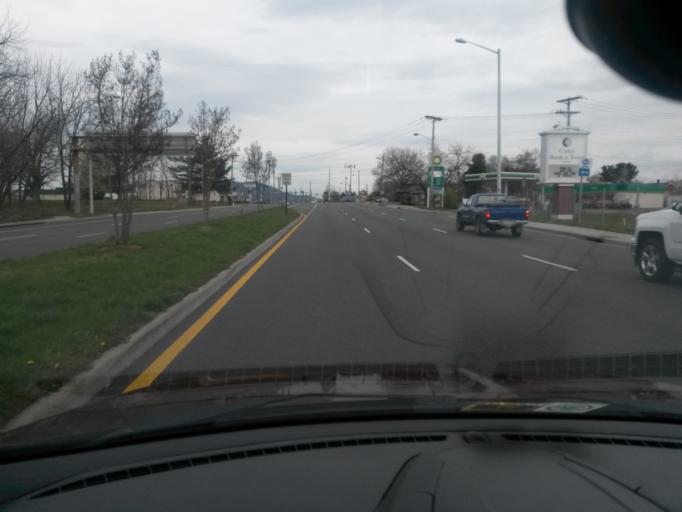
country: US
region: Virginia
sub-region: Roanoke County
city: Hollins
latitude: 37.3139
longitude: -79.9641
